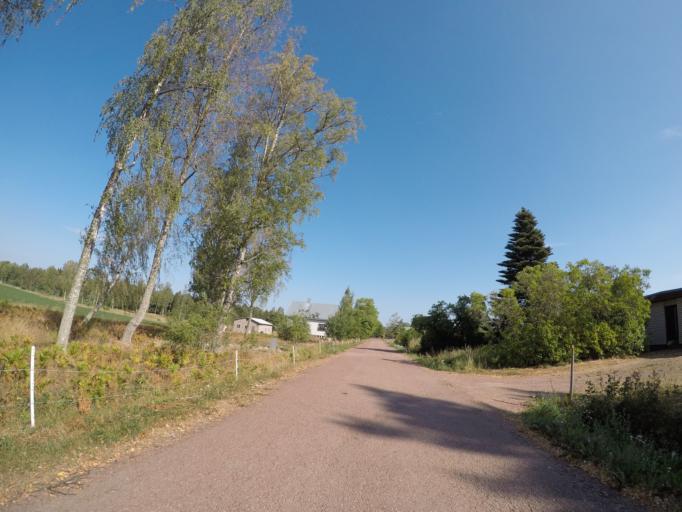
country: AX
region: Alands landsbygd
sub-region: Finstroem
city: Finstroem
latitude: 60.2795
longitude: 19.9569
